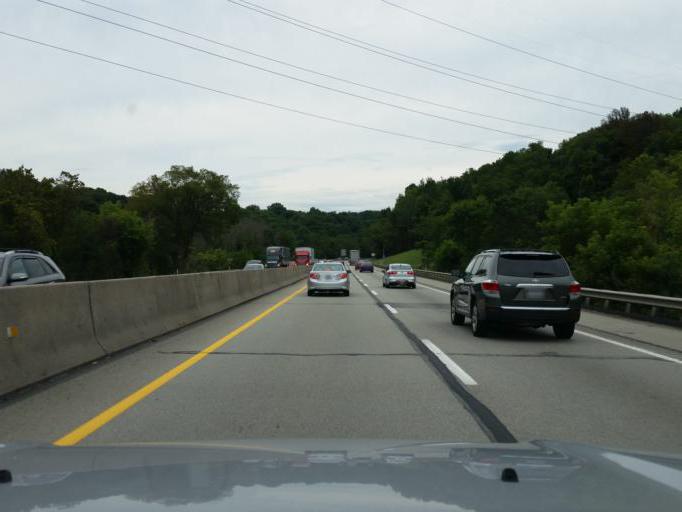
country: US
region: Pennsylvania
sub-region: Westmoreland County
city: Level Green
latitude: 40.4299
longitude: -79.7430
